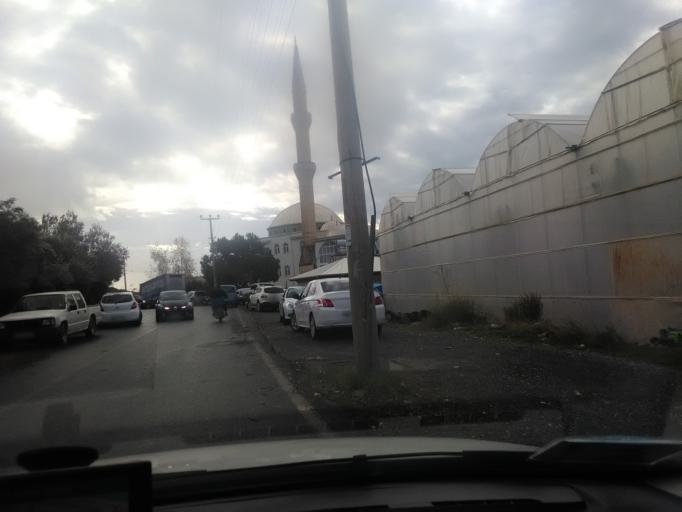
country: TR
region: Antalya
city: Gazipasa
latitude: 36.2509
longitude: 32.3030
